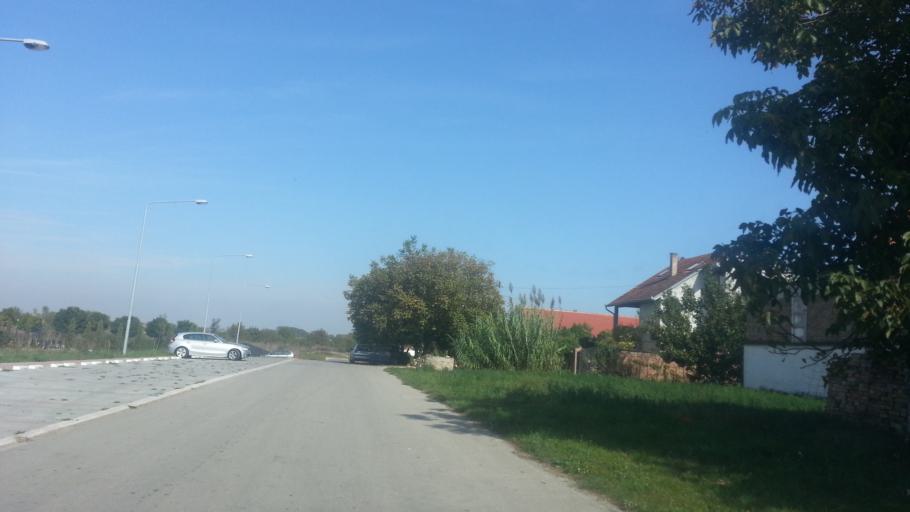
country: RS
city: Stari Banovci
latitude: 44.9940
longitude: 20.2891
